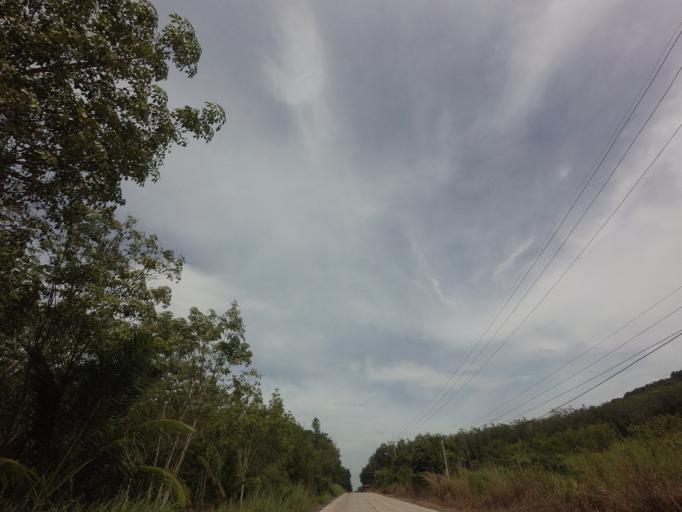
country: TH
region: Rayong
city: Klaeng
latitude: 12.6596
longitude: 101.5590
